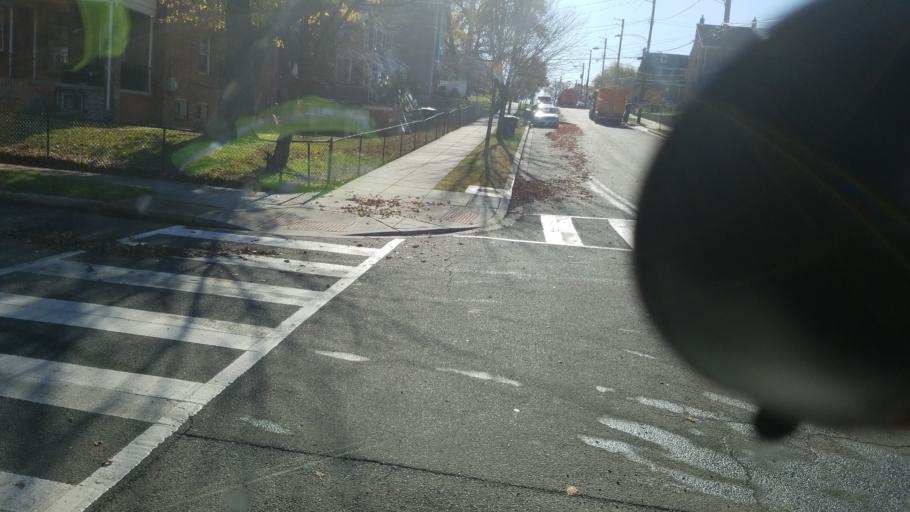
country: US
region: Maryland
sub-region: Prince George's County
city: Capitol Heights
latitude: 38.8920
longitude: -76.9472
